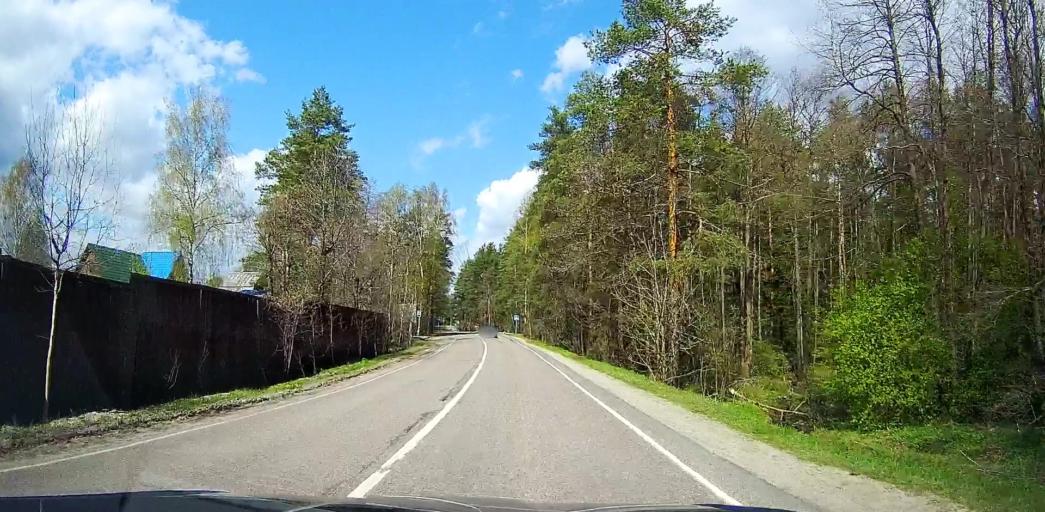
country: RU
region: Moskovskaya
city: Davydovo
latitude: 55.5699
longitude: 38.8232
